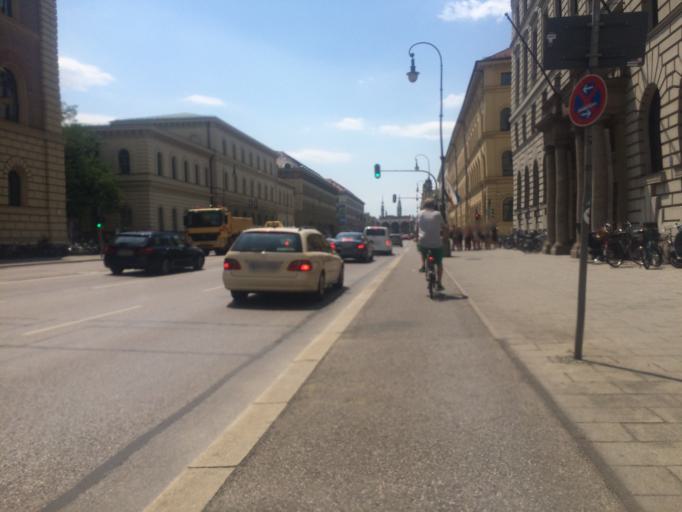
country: DE
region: Bavaria
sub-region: Upper Bavaria
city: Munich
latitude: 48.1474
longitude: 11.5797
